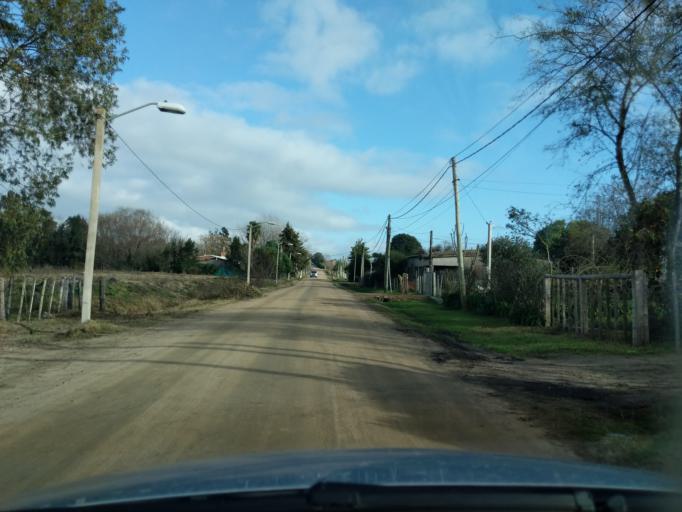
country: UY
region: Florida
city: Florida
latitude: -34.0809
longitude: -56.2076
